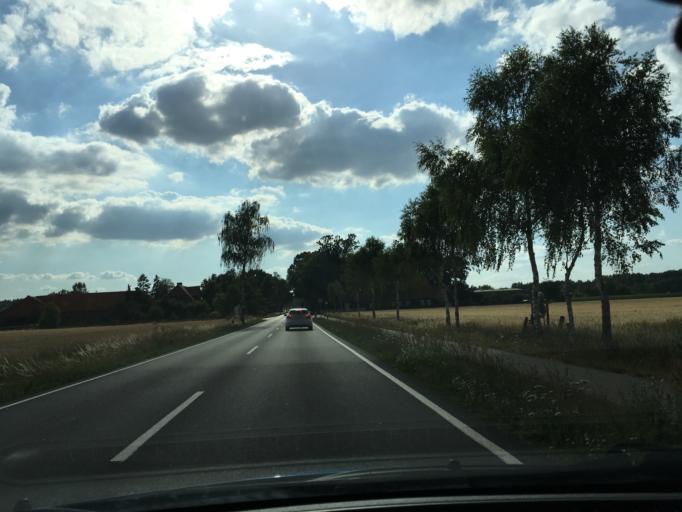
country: DE
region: Lower Saxony
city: Karwitz
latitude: 53.0839
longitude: 11.0184
